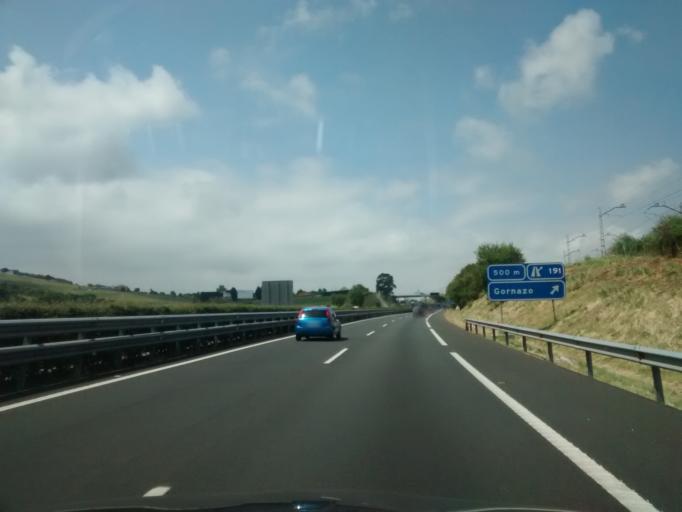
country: ES
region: Cantabria
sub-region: Provincia de Cantabria
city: Miengo
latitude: 43.4118
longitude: -3.9754
